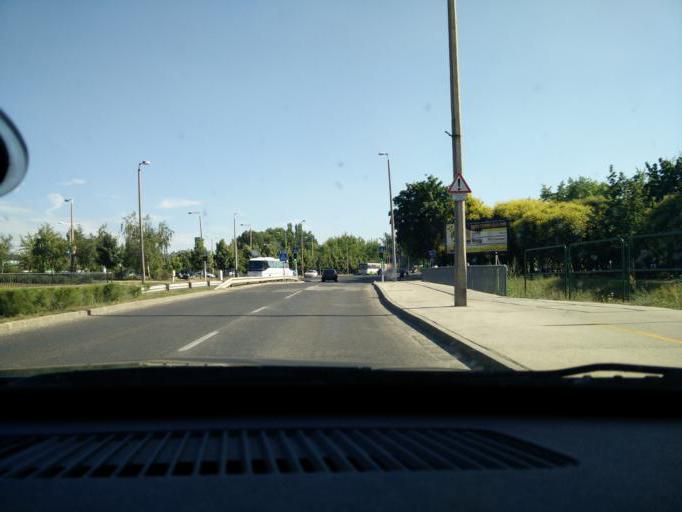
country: HU
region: Komarom-Esztergom
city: Tatabanya
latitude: 47.5718
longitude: 18.4091
